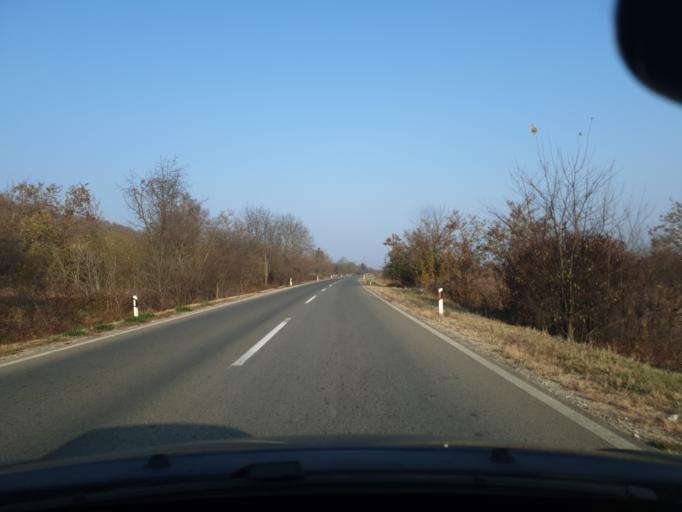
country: RS
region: Central Serbia
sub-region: Jablanicki Okrug
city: Leskovac
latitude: 42.9662
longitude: 21.9787
